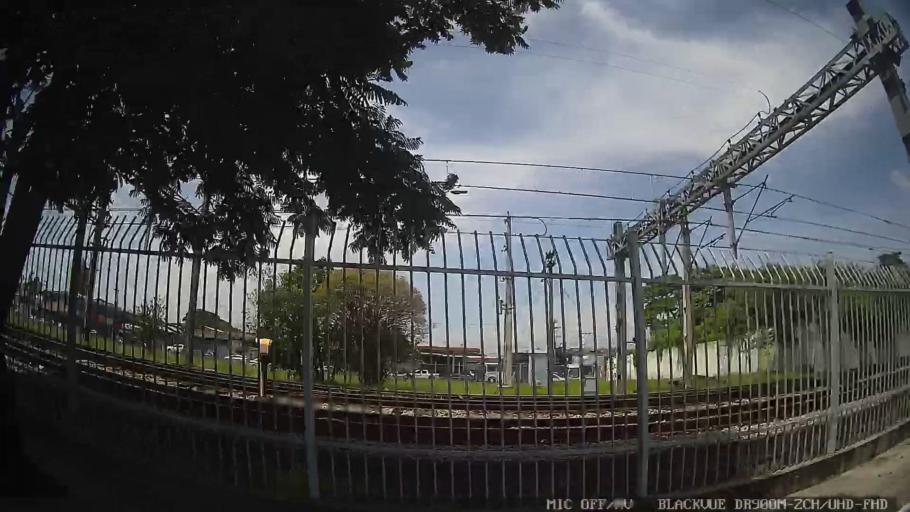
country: BR
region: Sao Paulo
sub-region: Suzano
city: Suzano
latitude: -23.5327
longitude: -46.3114
